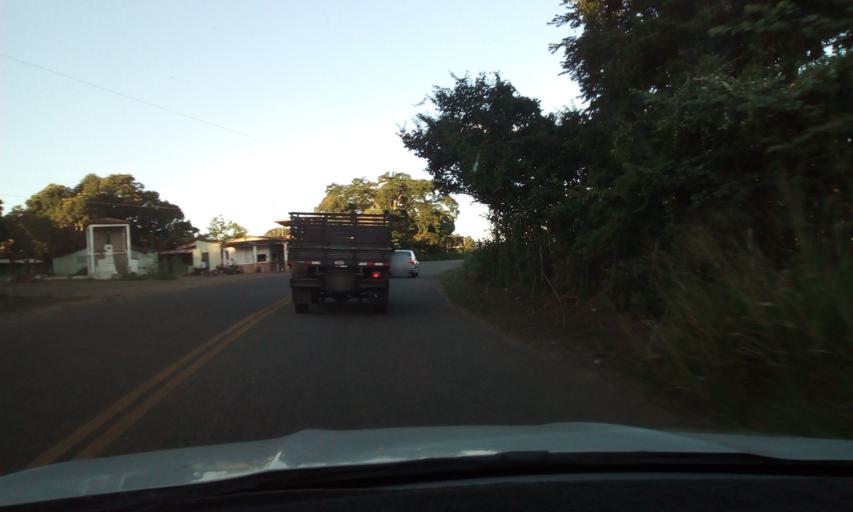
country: BR
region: Paraiba
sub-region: Areia
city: Remigio
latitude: -6.9632
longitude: -35.7524
